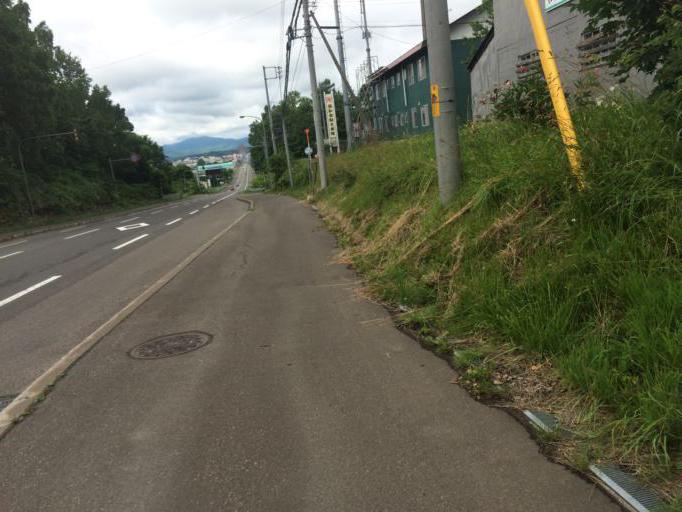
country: JP
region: Hokkaido
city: Niseko Town
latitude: 42.8756
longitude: 140.7504
